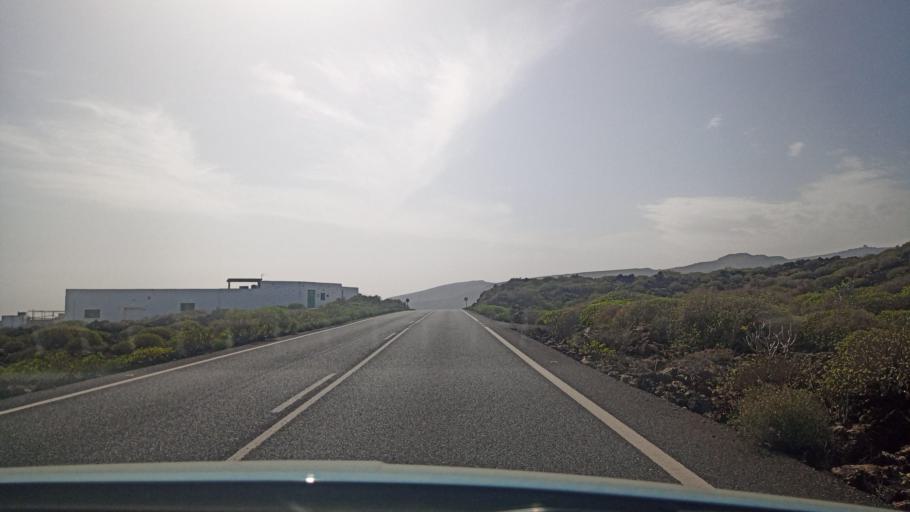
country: ES
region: Canary Islands
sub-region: Provincia de Las Palmas
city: Haria
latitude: 29.1442
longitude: -13.4525
